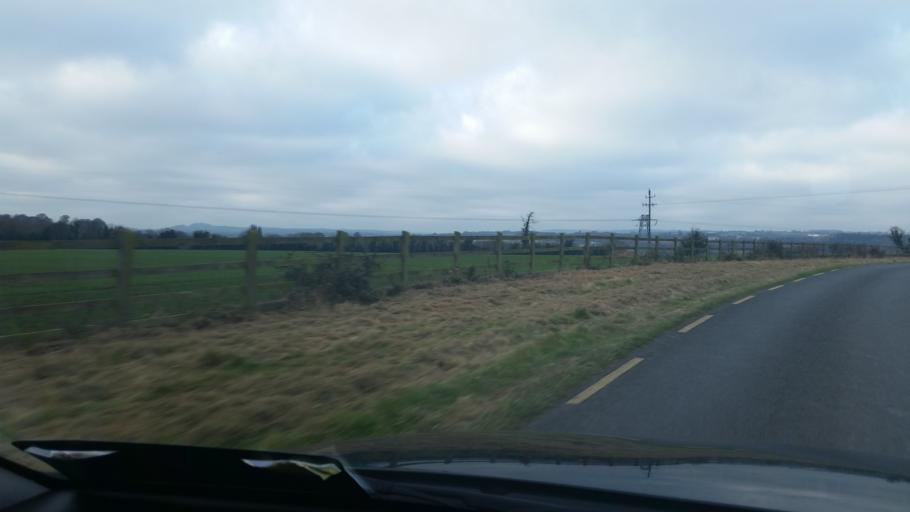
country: IE
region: Leinster
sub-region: Lu
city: Tullyallen
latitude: 53.7106
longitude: -6.4130
